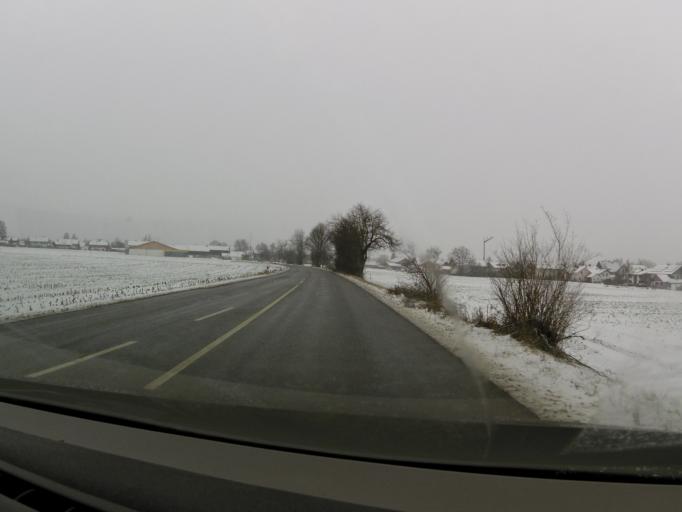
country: DE
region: Bavaria
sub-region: Upper Bavaria
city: Bichl
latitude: 47.7257
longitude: 11.4143
